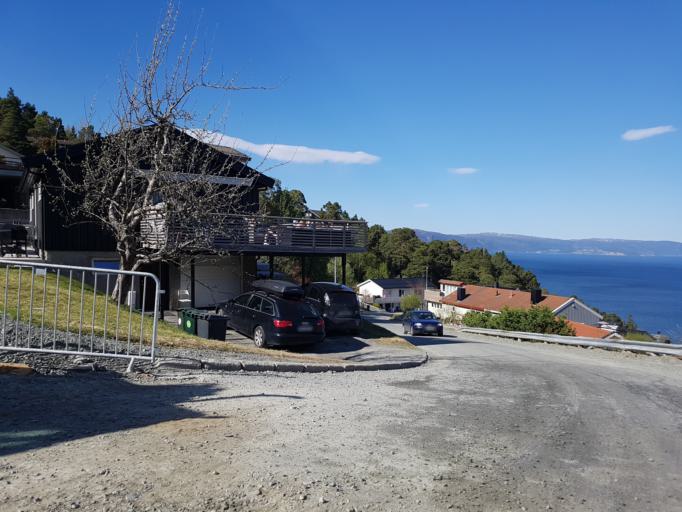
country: NO
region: Sor-Trondelag
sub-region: Trondheim
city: Trondheim
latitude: 63.4493
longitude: 10.3028
